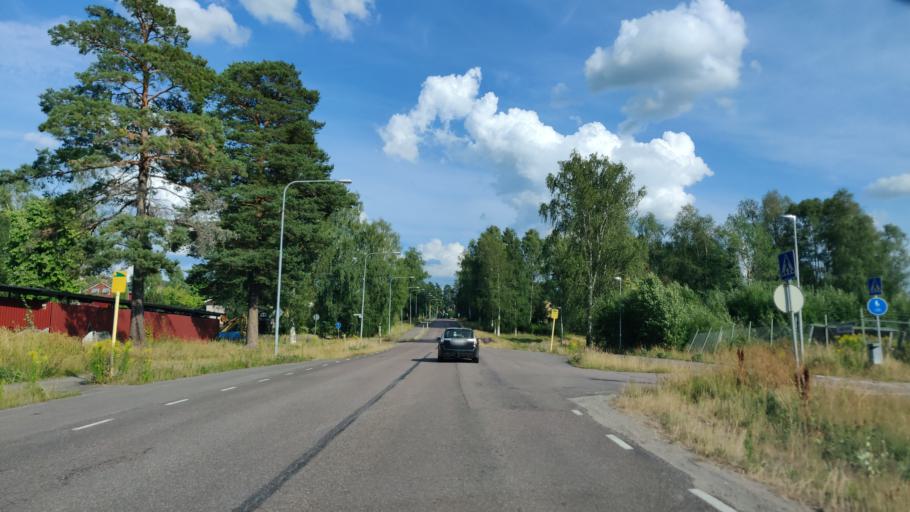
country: SE
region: Vaermland
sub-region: Hagfors Kommun
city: Hagfors
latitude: 60.0446
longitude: 13.6812
